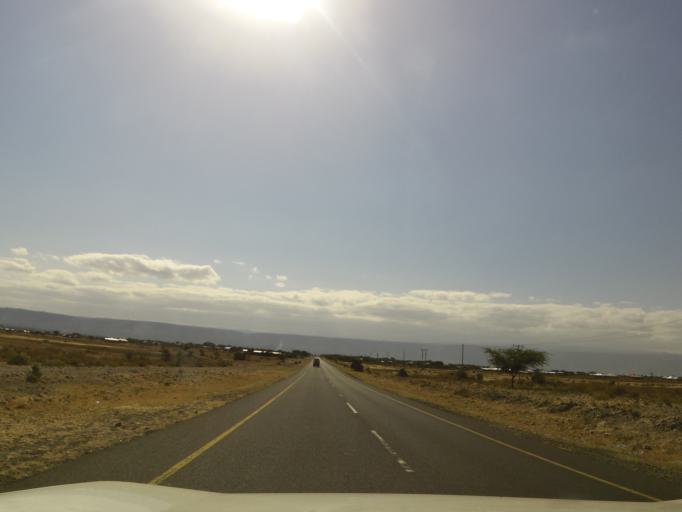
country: TZ
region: Arusha
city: Mto wa Mbu
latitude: -3.3926
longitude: 35.9025
